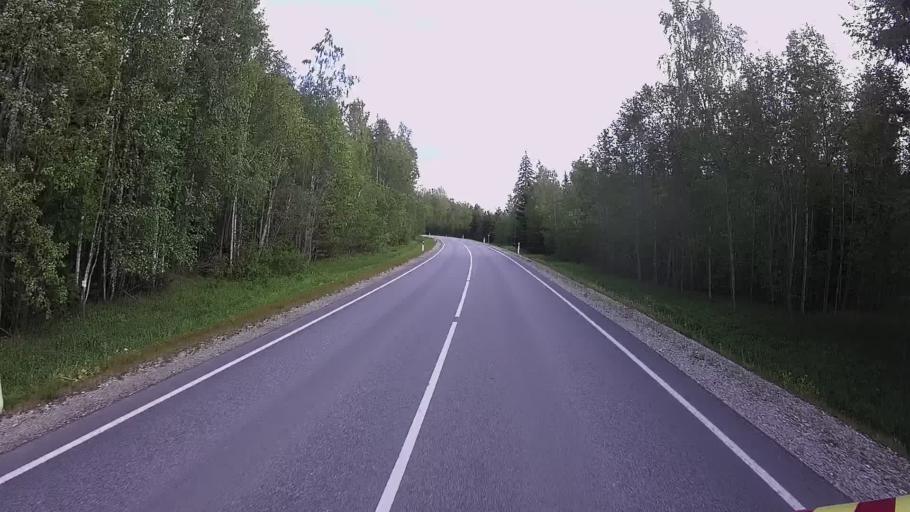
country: EE
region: Jogevamaa
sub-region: Mustvee linn
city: Mustvee
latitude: 58.8727
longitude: 26.8225
